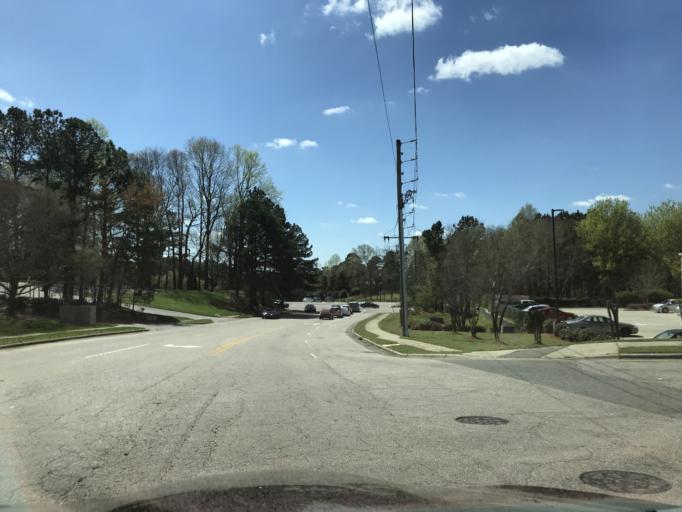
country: US
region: North Carolina
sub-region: Wake County
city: West Raleigh
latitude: 35.8672
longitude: -78.7161
